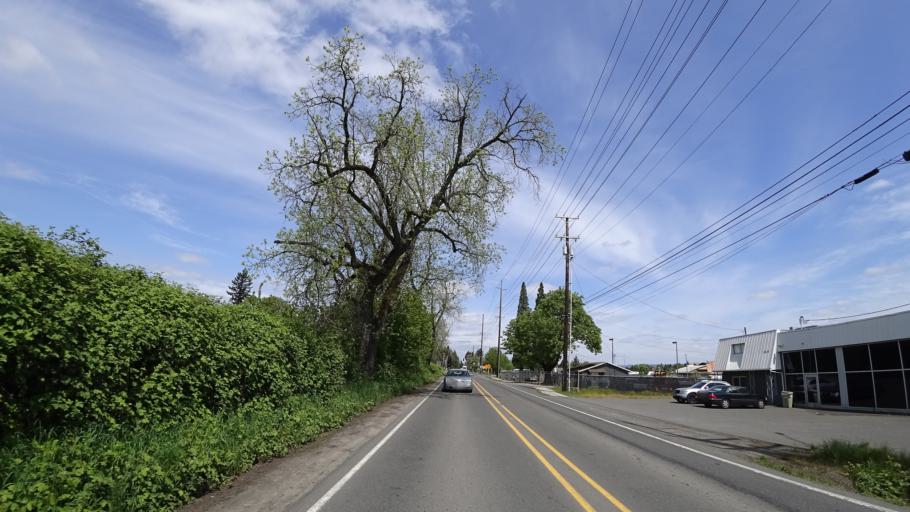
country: US
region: Oregon
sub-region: Washington County
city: Aloha
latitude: 45.4948
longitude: -122.8918
